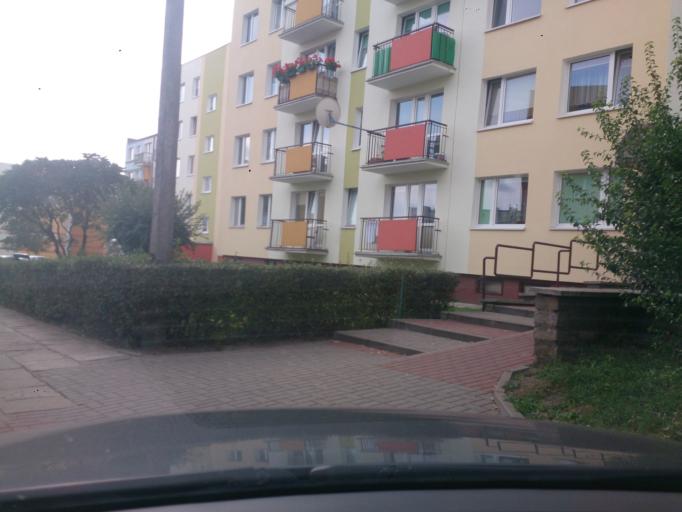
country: PL
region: Kujawsko-Pomorskie
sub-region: Grudziadz
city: Grudziadz
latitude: 53.4544
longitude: 18.7186
